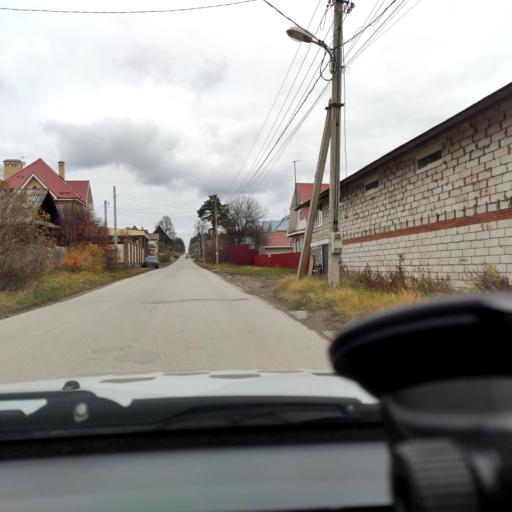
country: RU
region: Perm
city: Kondratovo
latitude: 58.0452
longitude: 56.1195
